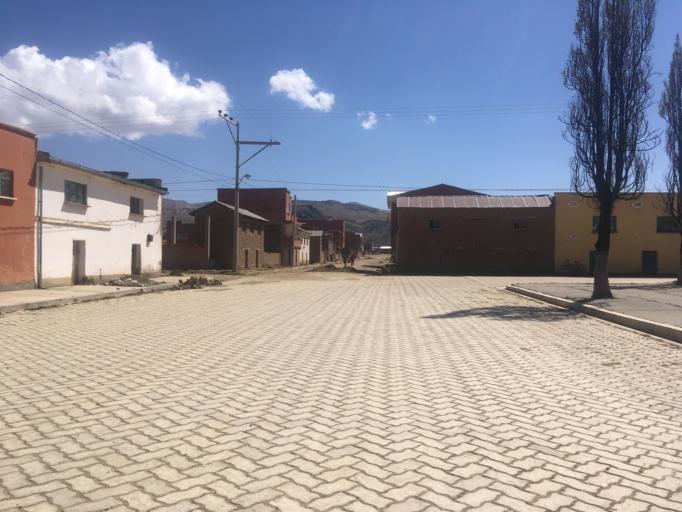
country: BO
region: La Paz
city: Huatajata
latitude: -16.1922
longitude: -68.7451
